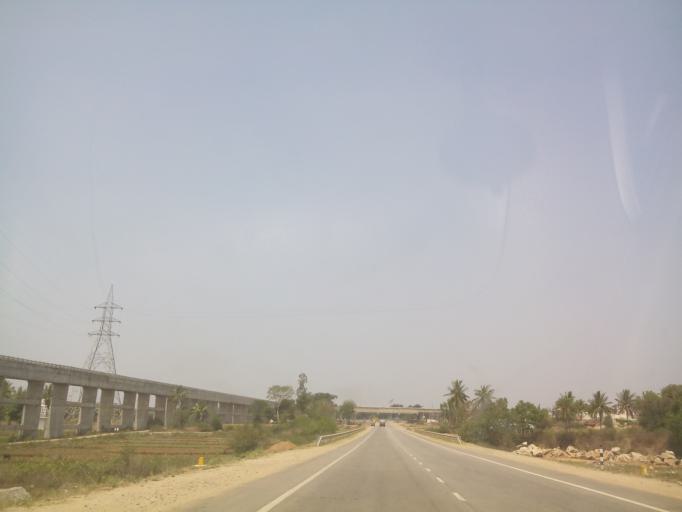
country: IN
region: Karnataka
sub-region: Hassan
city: Hassan
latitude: 12.9894
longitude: 76.0672
